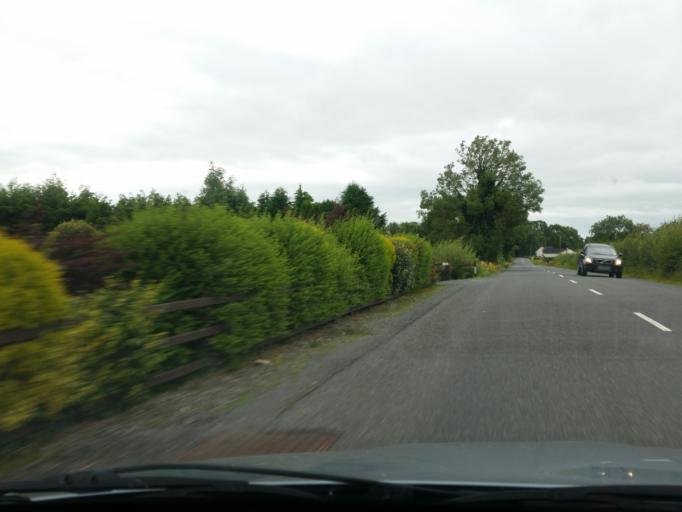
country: GB
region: Northern Ireland
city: Lisnaskea
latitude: 54.2223
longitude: -7.4616
